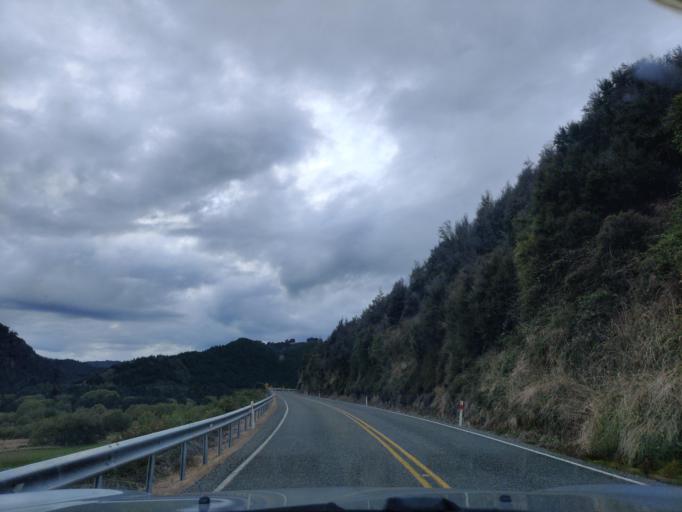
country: NZ
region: Tasman
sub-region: Tasman District
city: Wakefield
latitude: -41.7036
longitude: 172.6642
